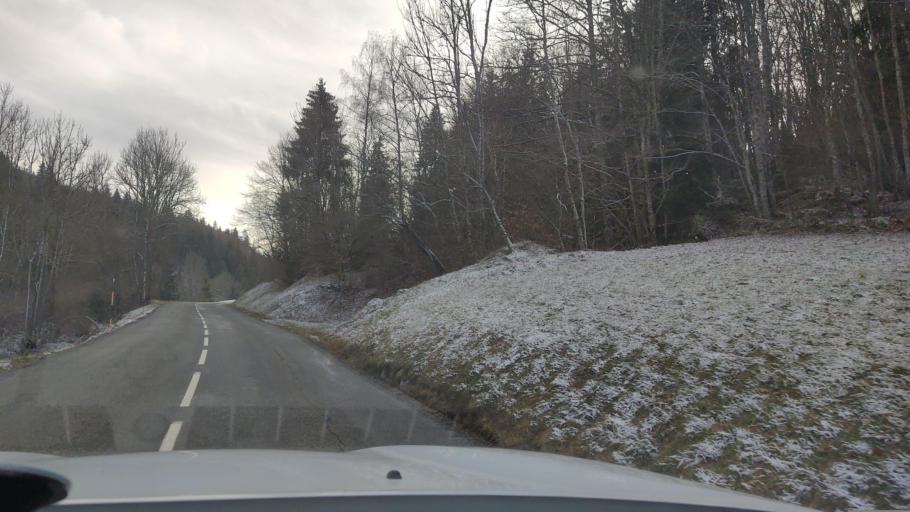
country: FR
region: Rhone-Alpes
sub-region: Departement de la Savoie
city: Coise-Saint-Jean-Pied-Gauthier
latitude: 45.5898
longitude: 6.1378
